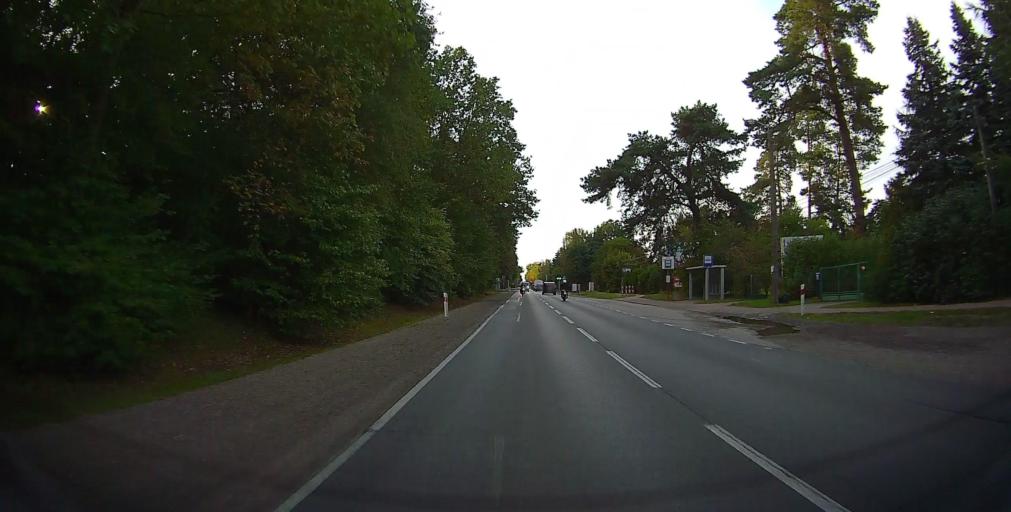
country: PL
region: Masovian Voivodeship
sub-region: Powiat piaseczynski
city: Zabieniec
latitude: 52.0513
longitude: 21.0636
